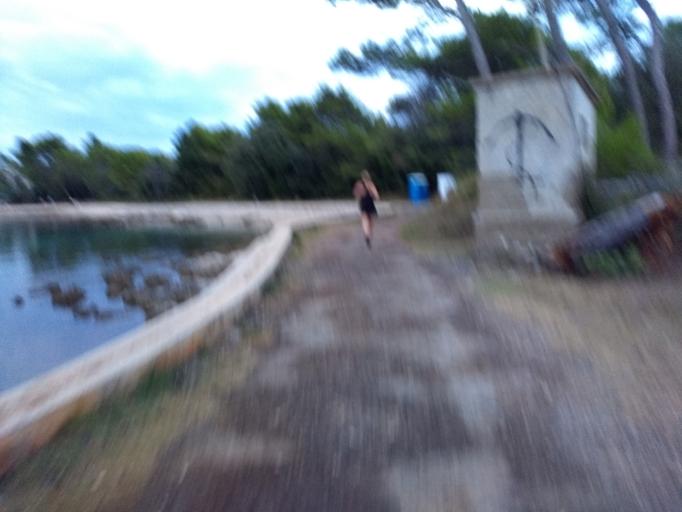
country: HR
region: Zadarska
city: Ugljan
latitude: 44.1346
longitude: 15.0689
